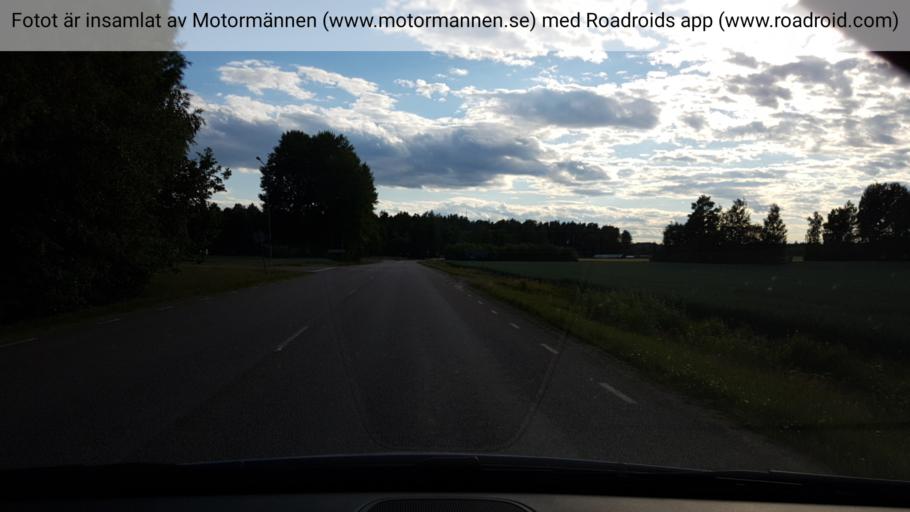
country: SE
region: Vaestmanland
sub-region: Vasteras
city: Hokasen
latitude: 59.6758
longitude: 16.5874
